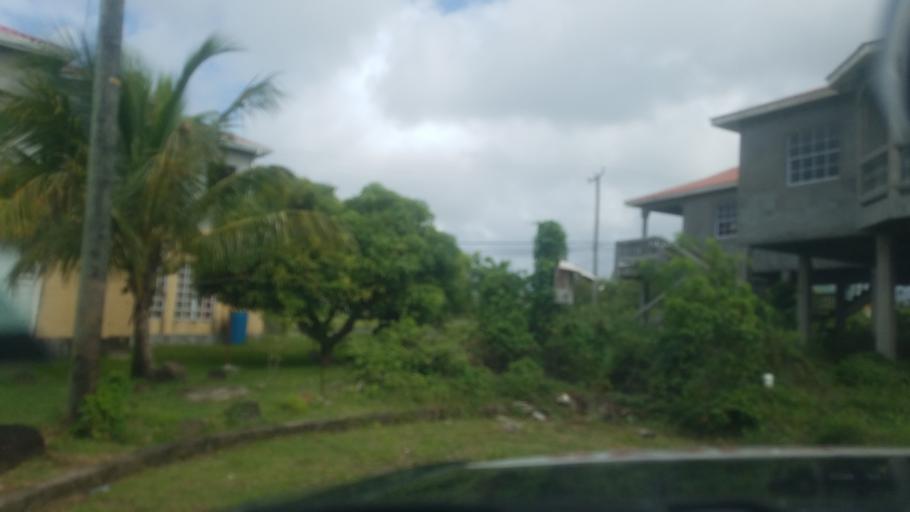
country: LC
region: Laborie Quarter
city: Laborie
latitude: 13.7484
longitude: -60.9747
